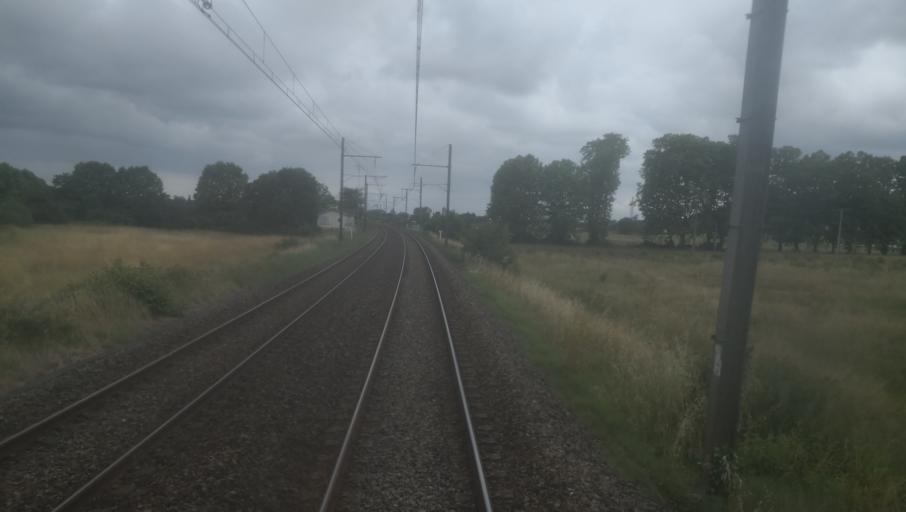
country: FR
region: Midi-Pyrenees
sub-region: Departement du Tarn-et-Garonne
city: Auvillar
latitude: 44.1004
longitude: 0.9488
